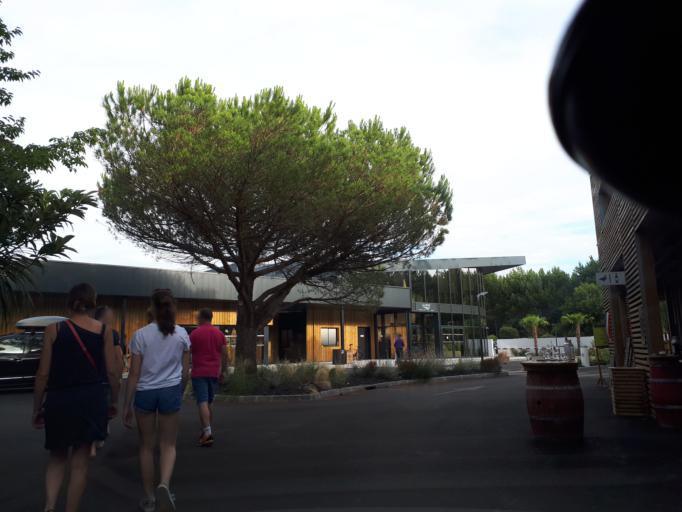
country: FR
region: Aquitaine
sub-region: Departement des Landes
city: Sanguinet
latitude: 44.4610
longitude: -1.1308
